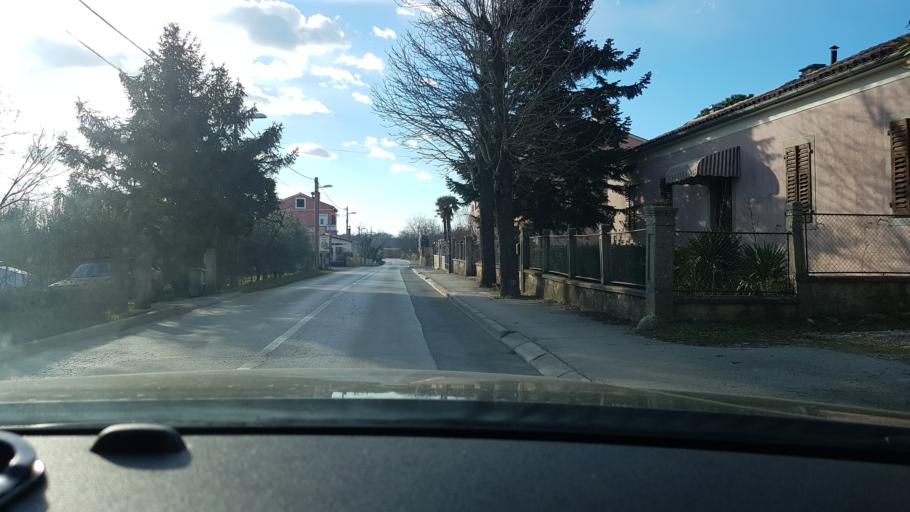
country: HR
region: Istarska
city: Vinez
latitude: 45.0988
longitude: 14.1108
